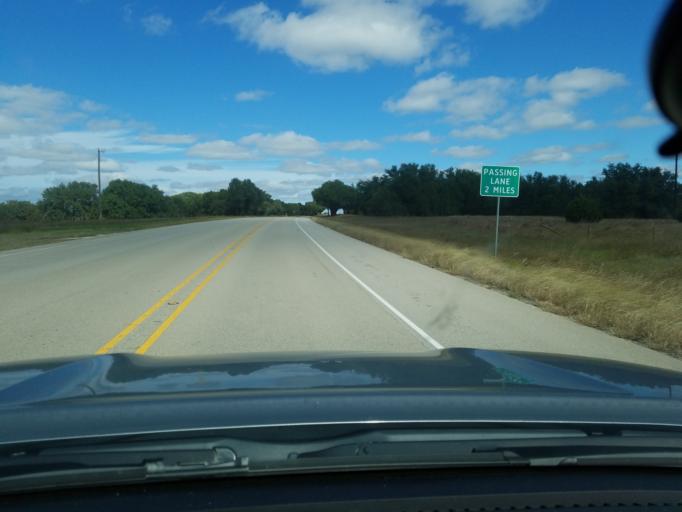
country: US
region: Texas
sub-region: Hamilton County
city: Hamilton
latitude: 31.6162
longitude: -98.1587
